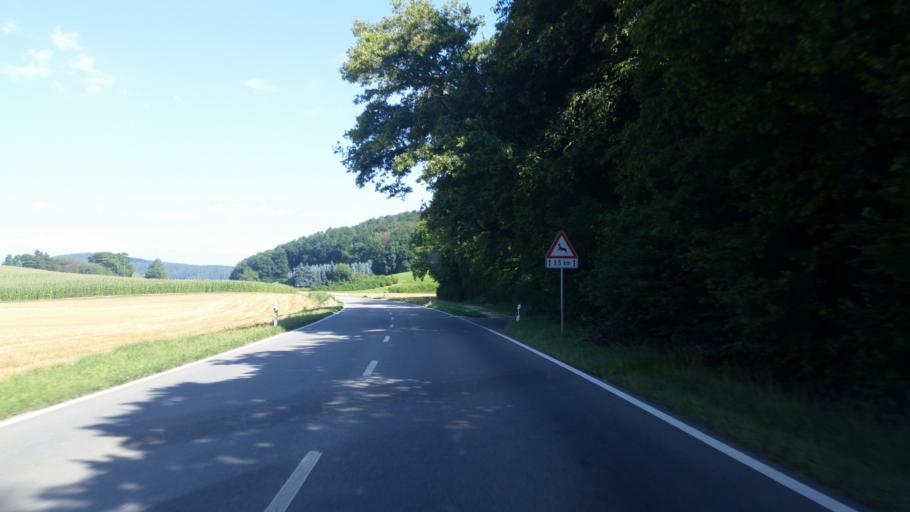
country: CH
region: Zurich
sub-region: Bezirk Buelach
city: Hochfelden
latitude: 47.5263
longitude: 8.4917
